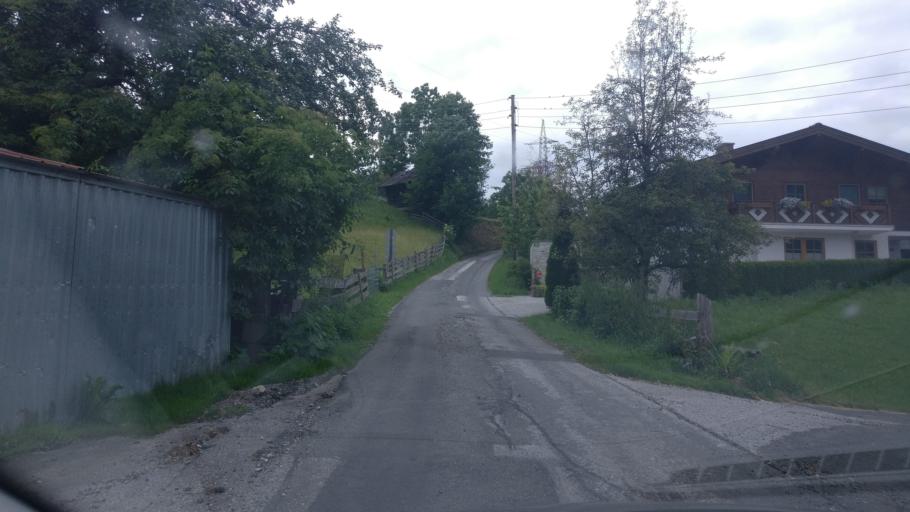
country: AT
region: Salzburg
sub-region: Politischer Bezirk Zell am See
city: Lend
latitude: 47.2947
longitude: 13.0454
